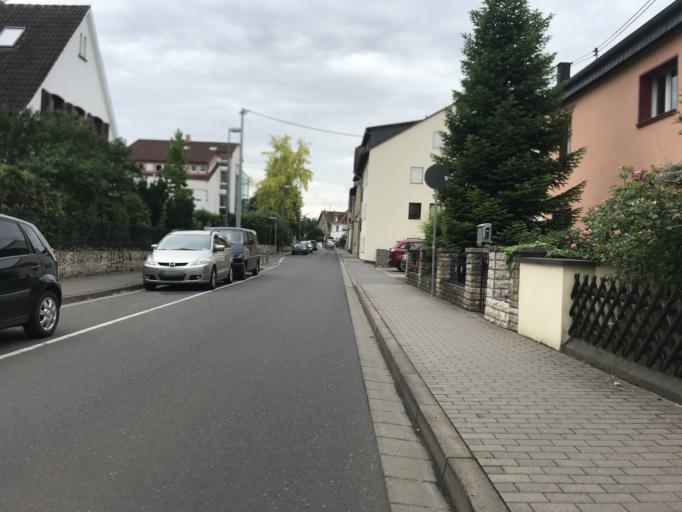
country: DE
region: Rheinland-Pfalz
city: Ingelheim am Rhein
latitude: 49.9686
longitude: 8.0615
